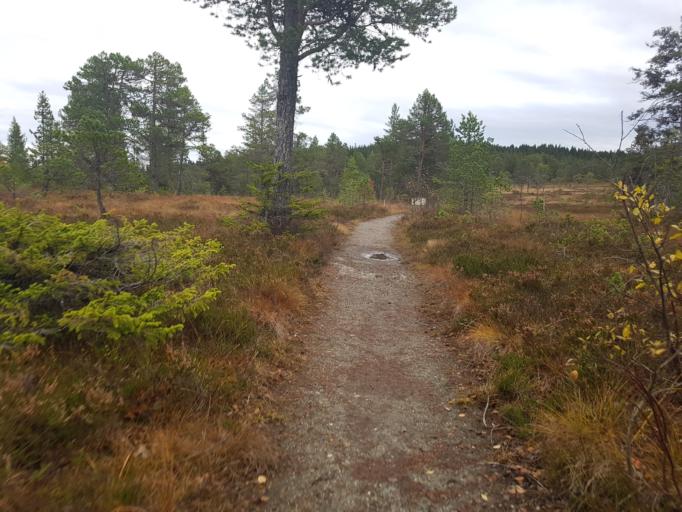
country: NO
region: Sor-Trondelag
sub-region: Melhus
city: Melhus
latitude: 63.3844
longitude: 10.2448
